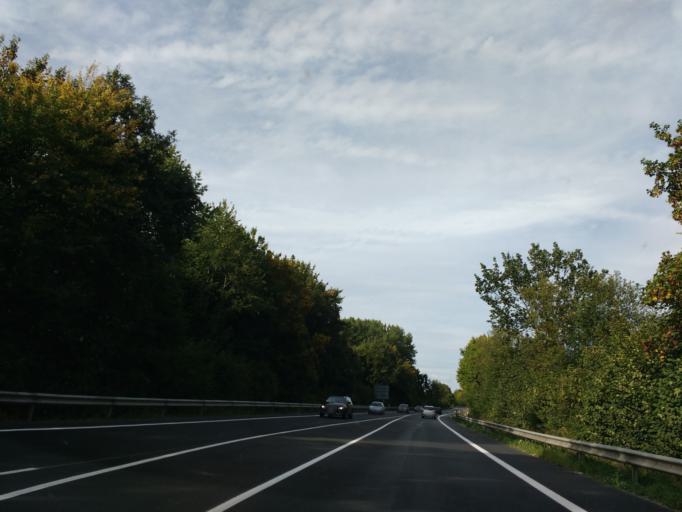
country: DE
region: North Rhine-Westphalia
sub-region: Regierungsbezirk Detmold
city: Steinheim
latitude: 51.8993
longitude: 9.0861
